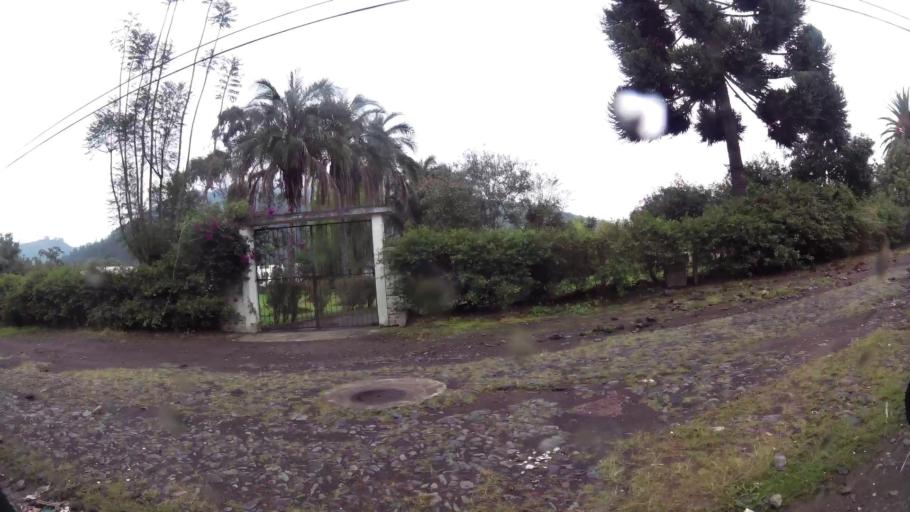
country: EC
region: Pichincha
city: Sangolqui
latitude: -0.2845
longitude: -78.4507
